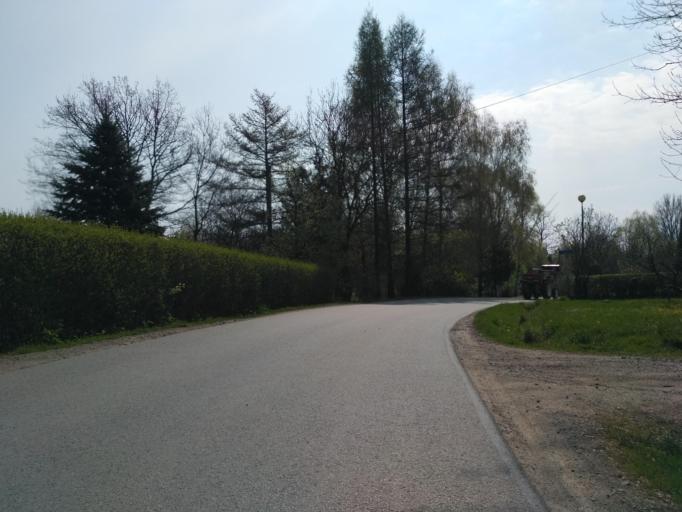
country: PL
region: Subcarpathian Voivodeship
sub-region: Krosno
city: Krosno
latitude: 49.6658
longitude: 21.7479
